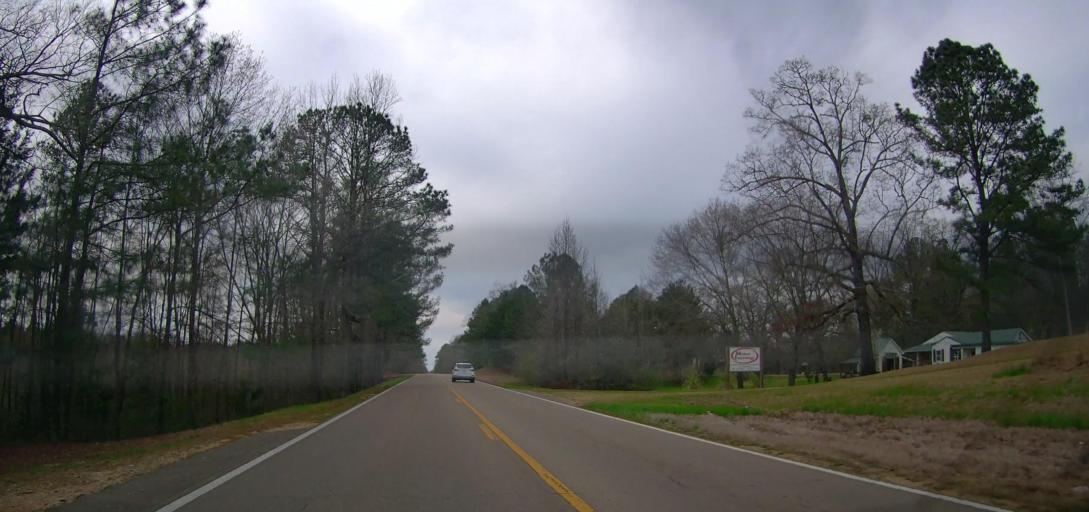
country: US
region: Mississippi
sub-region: Itawamba County
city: Mantachie
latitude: 34.2569
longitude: -88.5007
